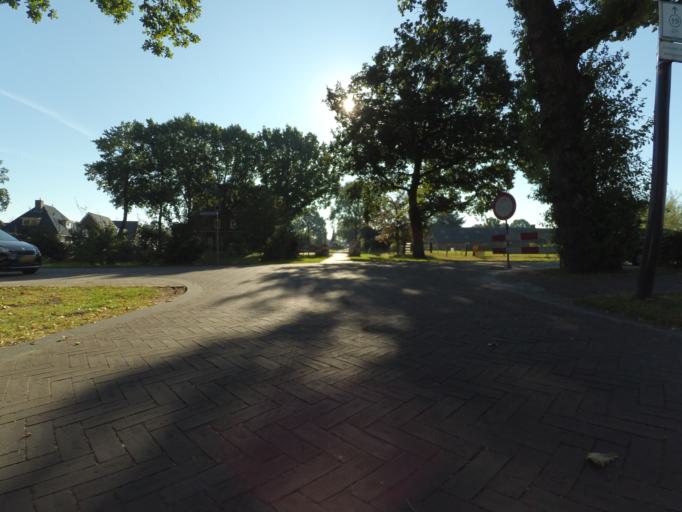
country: NL
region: Gelderland
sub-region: Gemeente Putten
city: Putten
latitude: 52.2576
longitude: 5.5838
